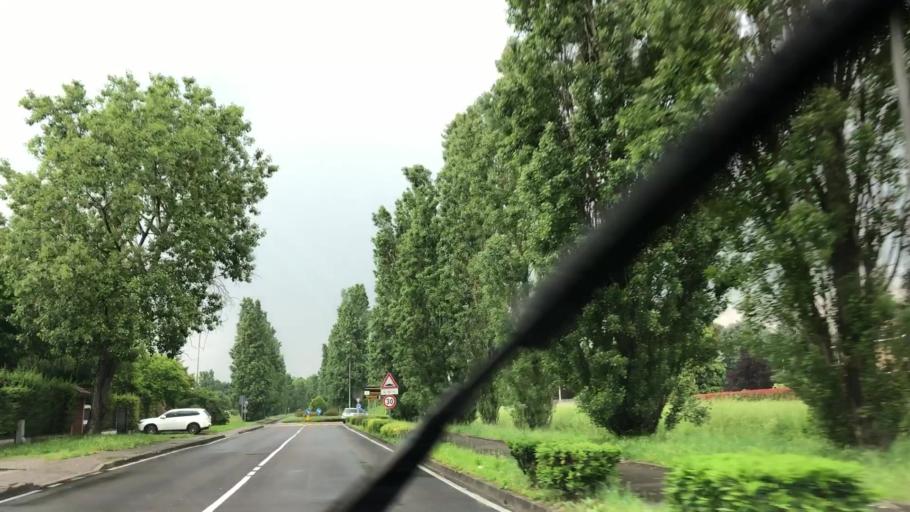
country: IT
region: Lombardy
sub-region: Citta metropolitana di Milano
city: Paderno Dugnano
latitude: 45.5767
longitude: 9.1684
